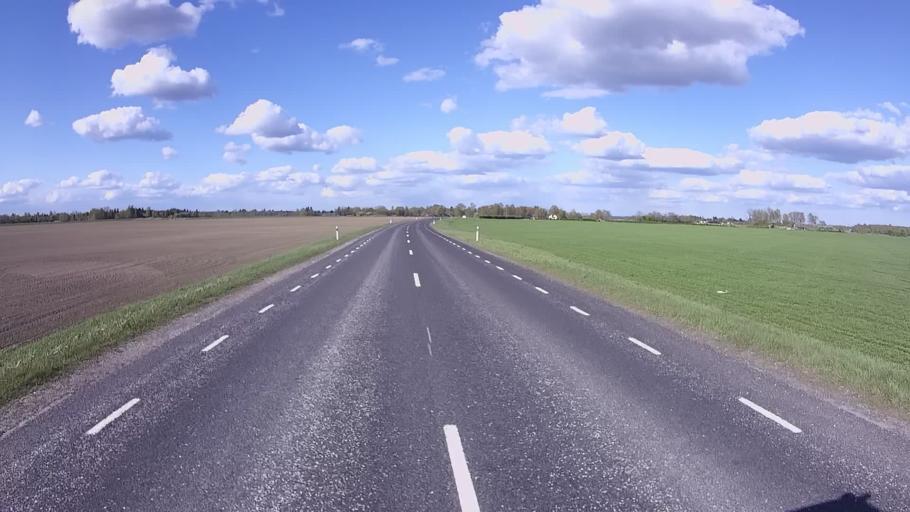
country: EE
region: Jogevamaa
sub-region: Jogeva linn
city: Jogeva
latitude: 58.7225
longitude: 26.1892
